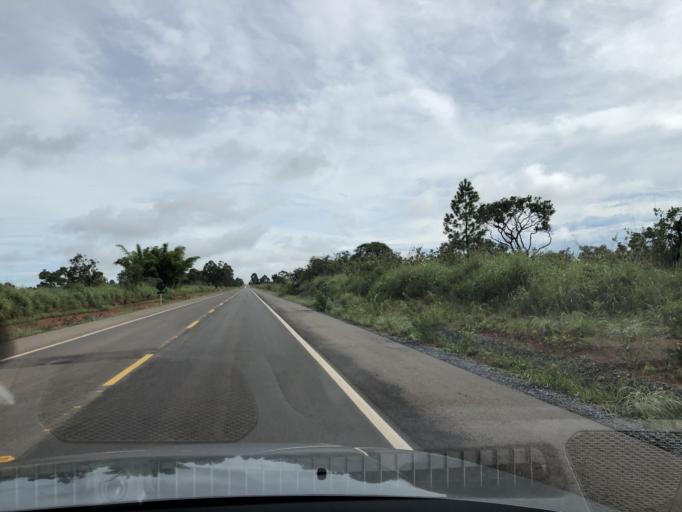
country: BR
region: Federal District
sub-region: Brasilia
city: Brasilia
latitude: -15.6619
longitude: -48.0851
